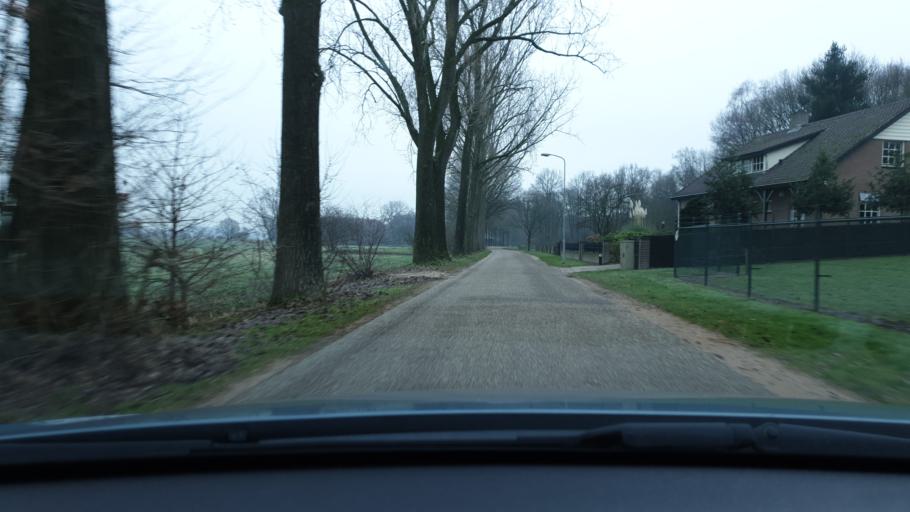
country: NL
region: Gelderland
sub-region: Gemeente Wijchen
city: Bergharen
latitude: 51.8632
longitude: 5.6690
